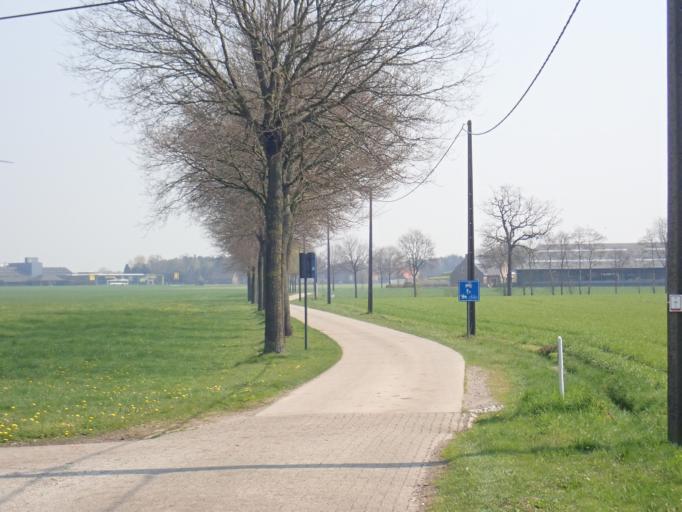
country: BE
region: Flanders
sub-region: Provincie Antwerpen
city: Essen
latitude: 51.4385
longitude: 4.4913
